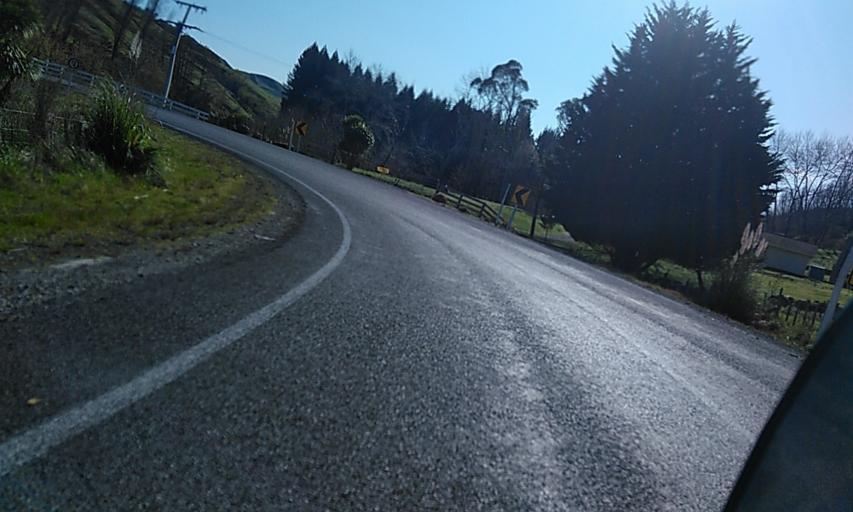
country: NZ
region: Gisborne
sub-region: Gisborne District
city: Gisborne
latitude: -38.5148
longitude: 178.0403
